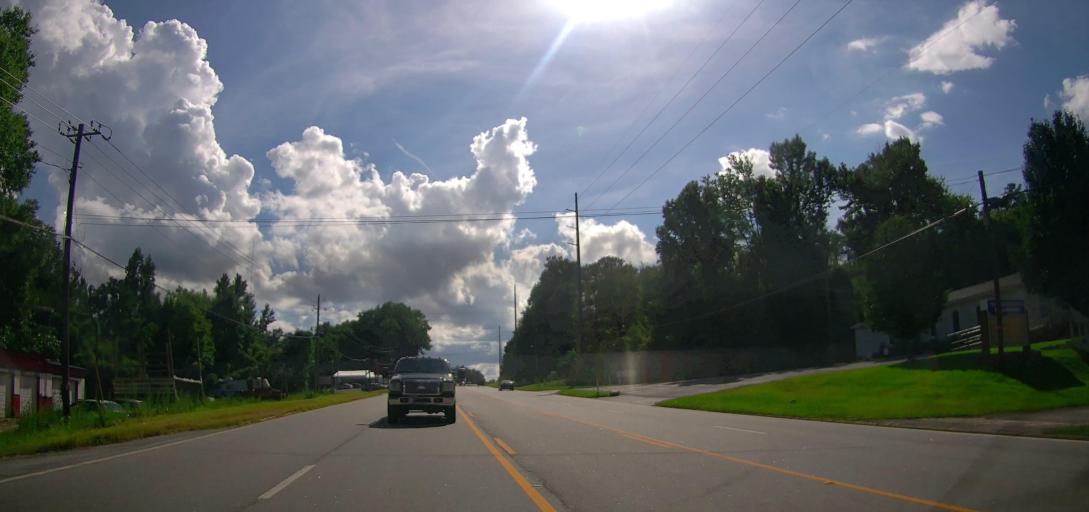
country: US
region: Alabama
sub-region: Russell County
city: Ladonia
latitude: 32.4731
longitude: -85.0466
